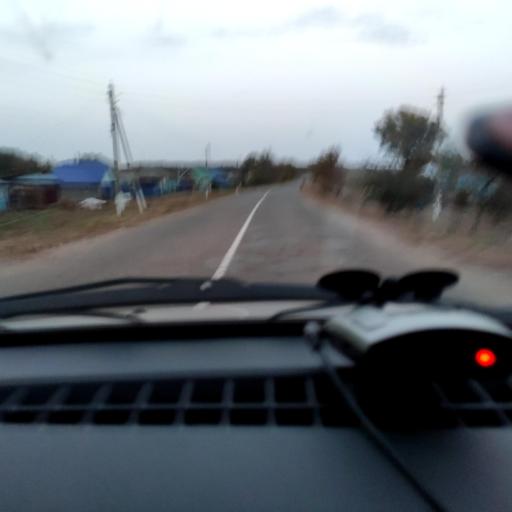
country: RU
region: Voronezj
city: Uryv-Pokrovka
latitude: 51.2316
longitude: 38.9276
